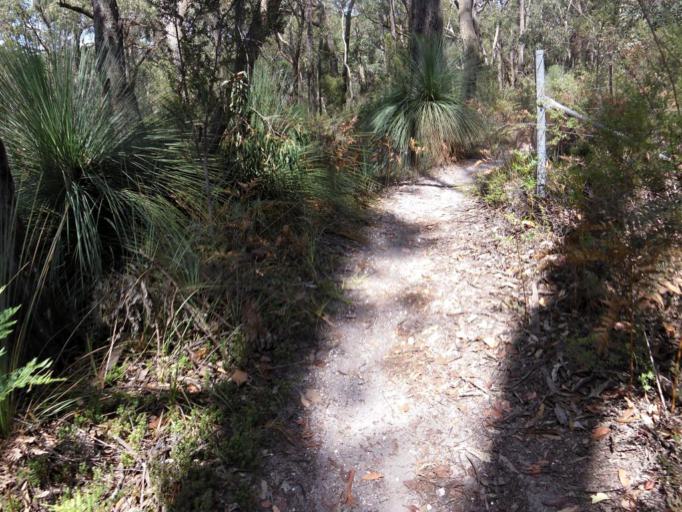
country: AU
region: Victoria
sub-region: Melton
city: Melton West
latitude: -37.5098
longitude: 144.5541
